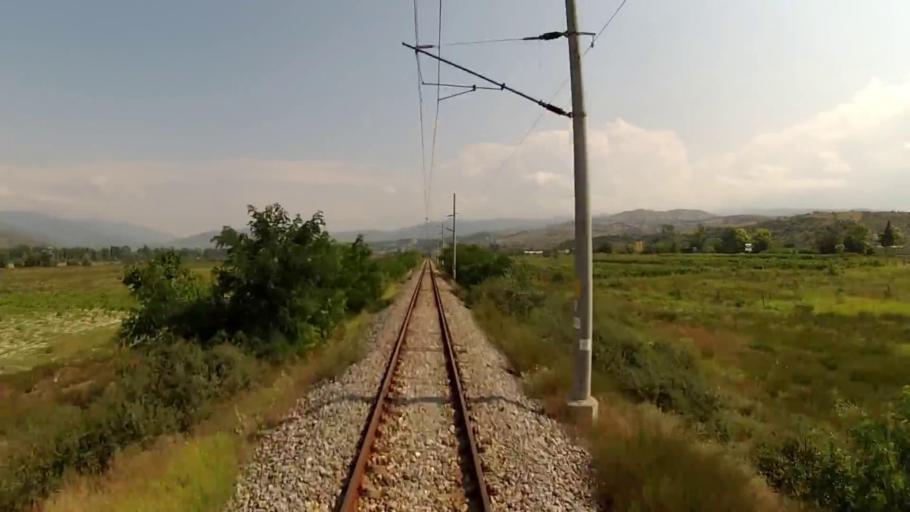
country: BG
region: Blagoevgrad
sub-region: Obshtina Strumyani
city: Strumyani
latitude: 41.6518
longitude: 23.1890
